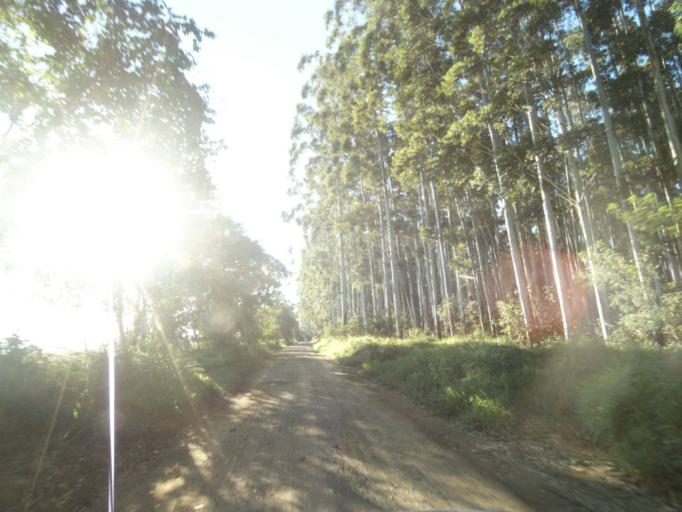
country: BR
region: Parana
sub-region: Tibagi
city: Tibagi
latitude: -24.5163
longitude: -50.6014
